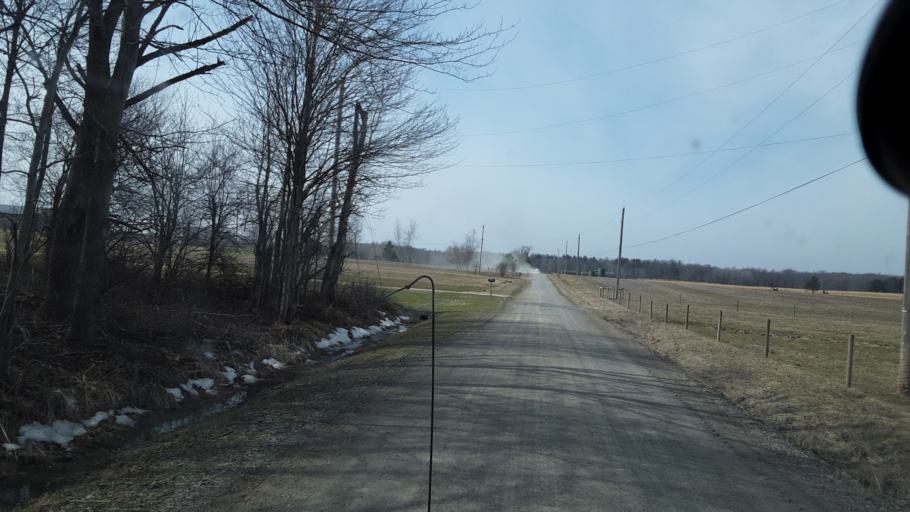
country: US
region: Ohio
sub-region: Ashtabula County
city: Andover
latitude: 41.6237
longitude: -80.6422
